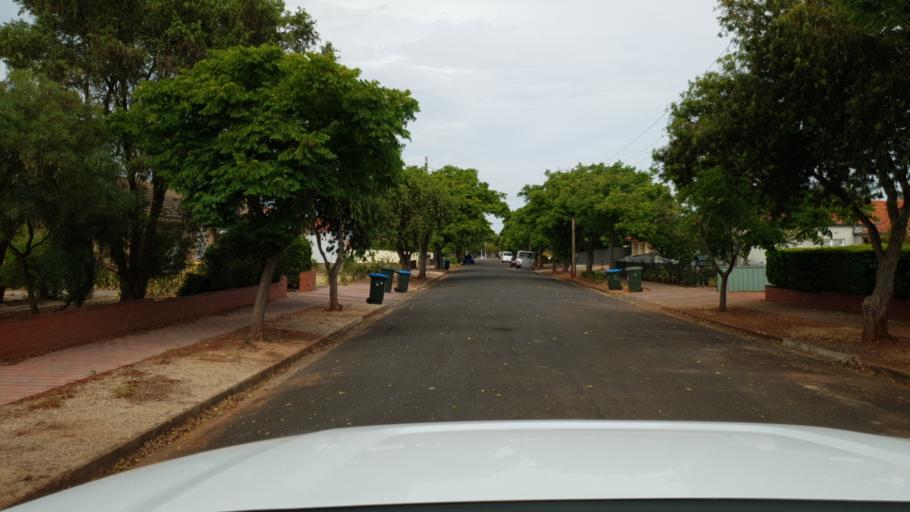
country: AU
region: South Australia
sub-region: Mitcham
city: Clarence Gardens
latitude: -34.9731
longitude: 138.5818
